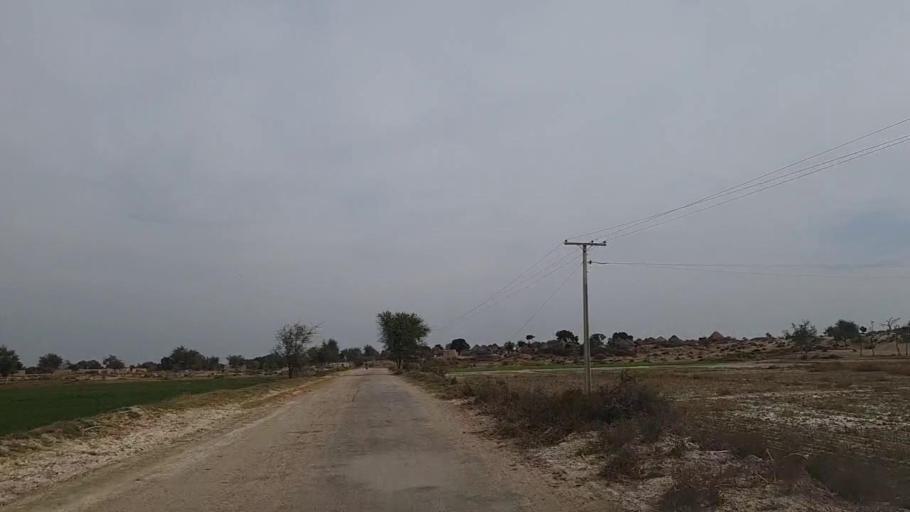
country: PK
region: Sindh
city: Jam Sahib
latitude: 26.4000
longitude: 68.5187
